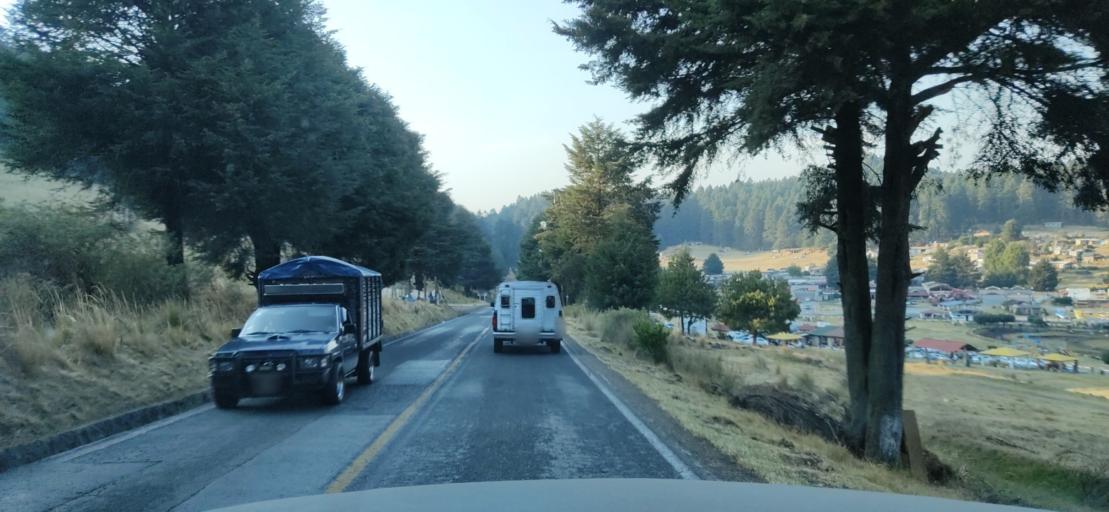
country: MX
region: Mexico
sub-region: Ocoyoacac
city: San Jeronimo Acazulco
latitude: 19.2769
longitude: -99.3798
